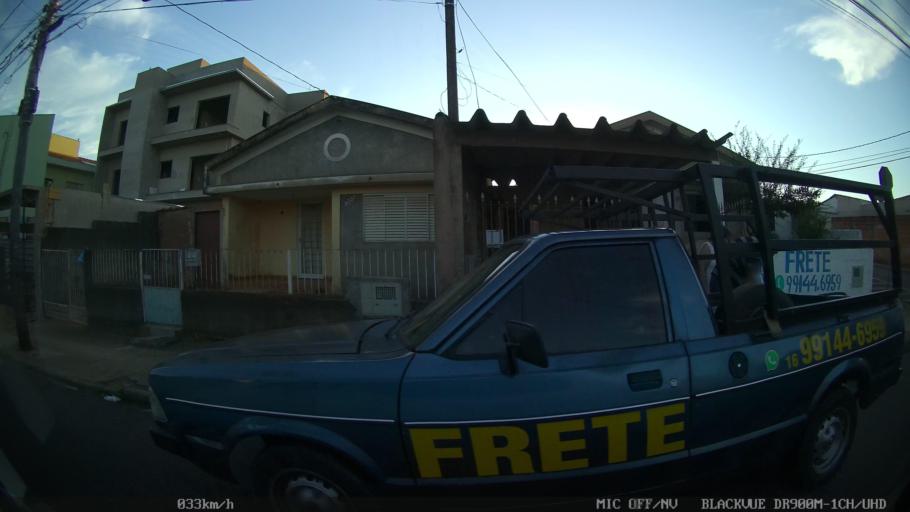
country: BR
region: Sao Paulo
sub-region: Franca
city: Franca
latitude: -20.5210
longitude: -47.4067
